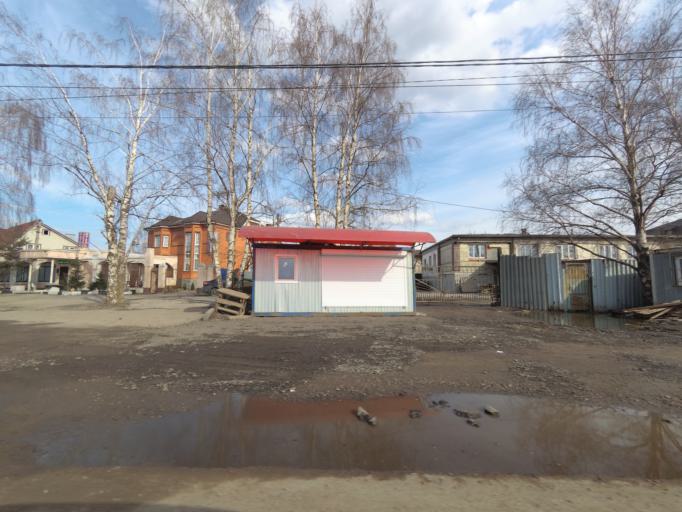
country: RU
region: Moskovskaya
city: Lobnya
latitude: 55.9919
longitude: 37.4171
